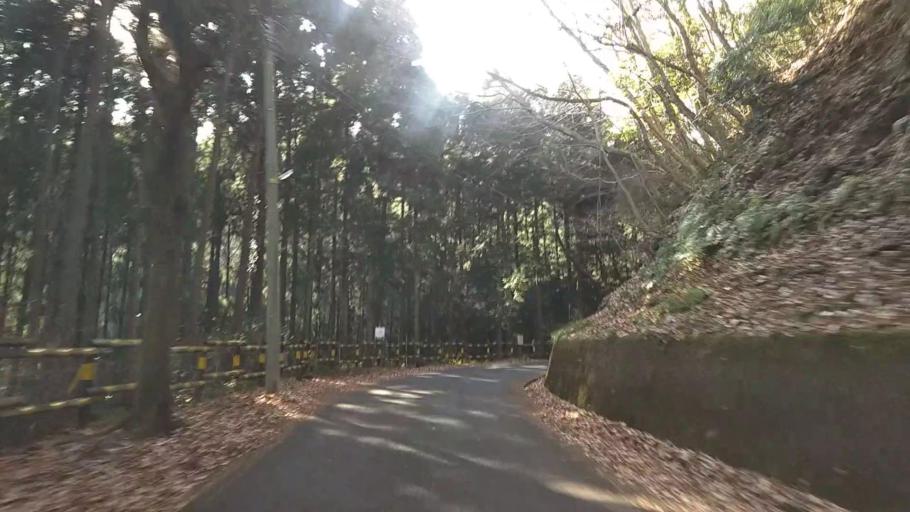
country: JP
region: Kanagawa
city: Isehara
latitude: 35.4461
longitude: 139.2861
